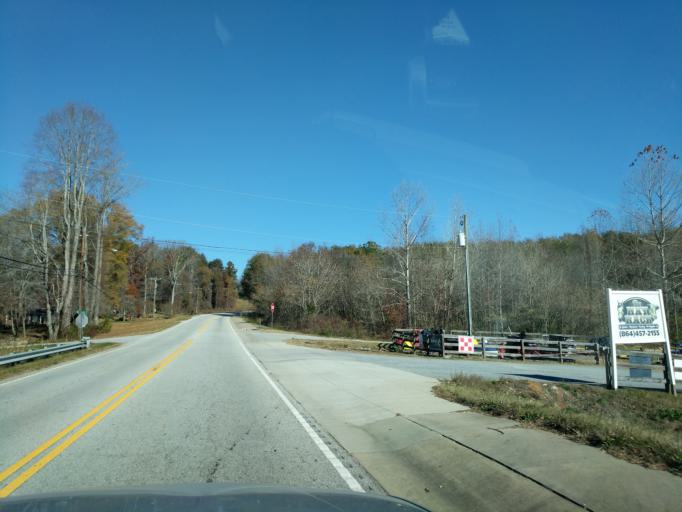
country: US
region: South Carolina
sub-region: Spartanburg County
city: Landrum
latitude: 35.1706
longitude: -82.1946
